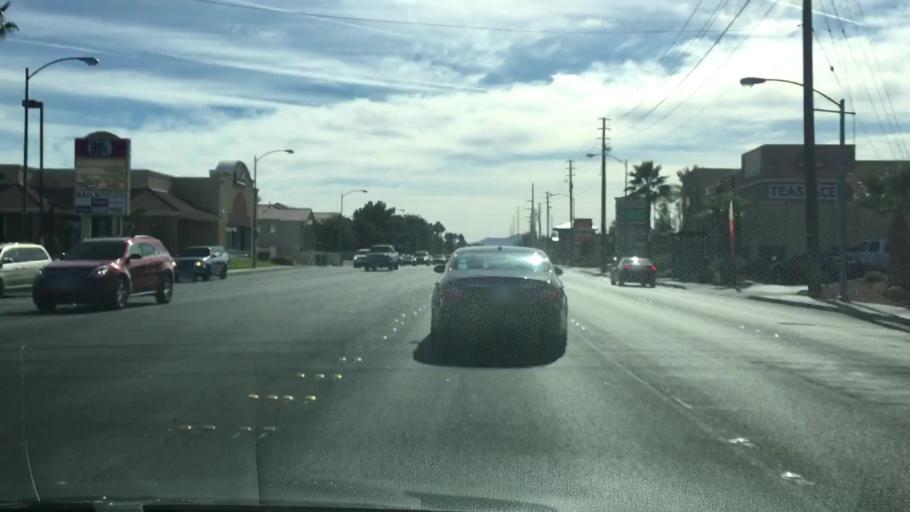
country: US
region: Nevada
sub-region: Clark County
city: Whitney
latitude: 36.0562
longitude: -115.1184
